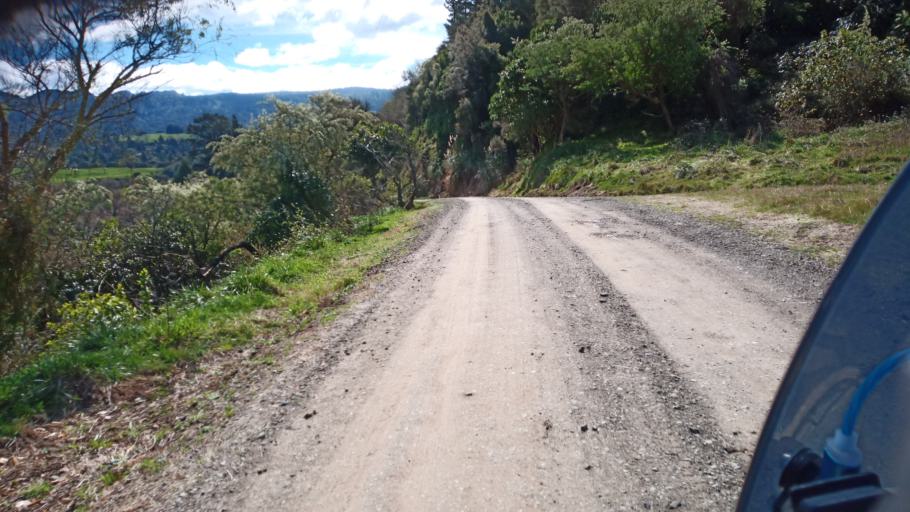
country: NZ
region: Hawke's Bay
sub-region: Wairoa District
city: Wairoa
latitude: -38.8343
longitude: 177.1627
